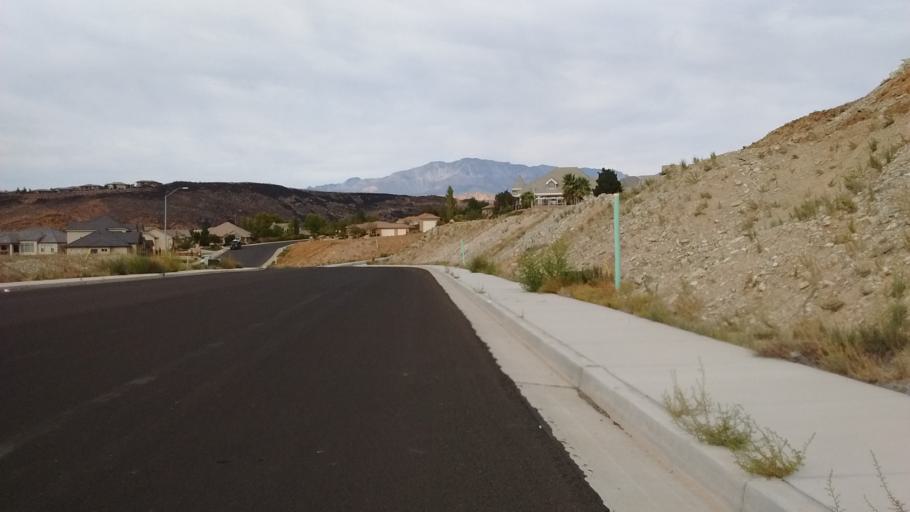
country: US
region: Utah
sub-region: Washington County
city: Washington
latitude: 37.1158
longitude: -113.4944
